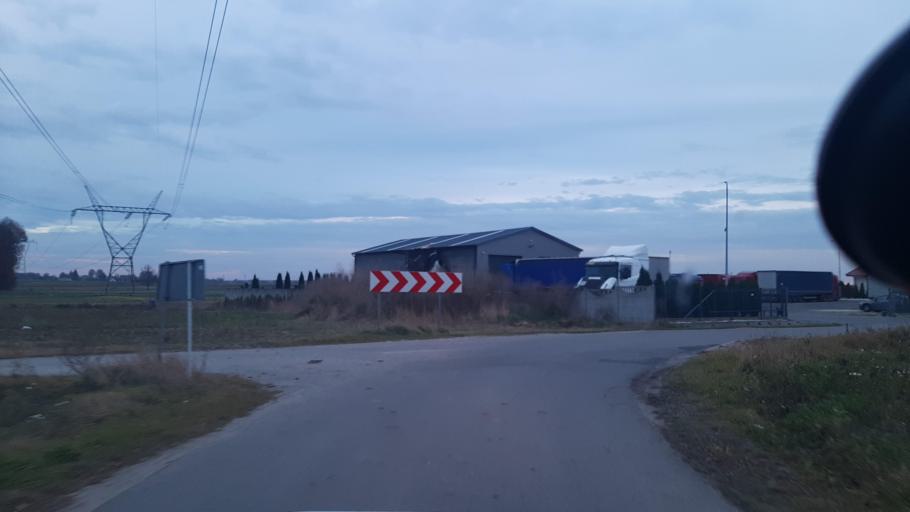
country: PL
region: Lublin Voivodeship
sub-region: Powiat lubelski
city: Garbow
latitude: 51.3689
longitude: 22.3849
